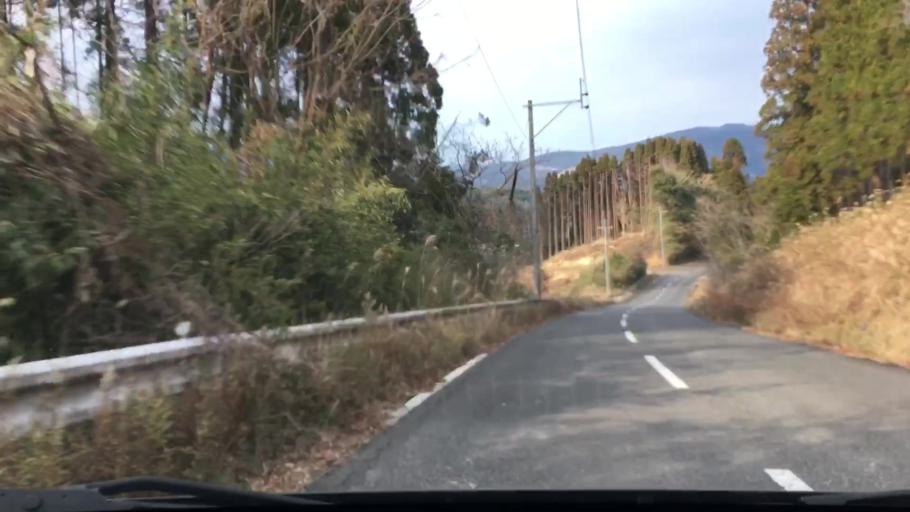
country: JP
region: Miyazaki
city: Nichinan
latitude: 31.6082
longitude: 131.3297
